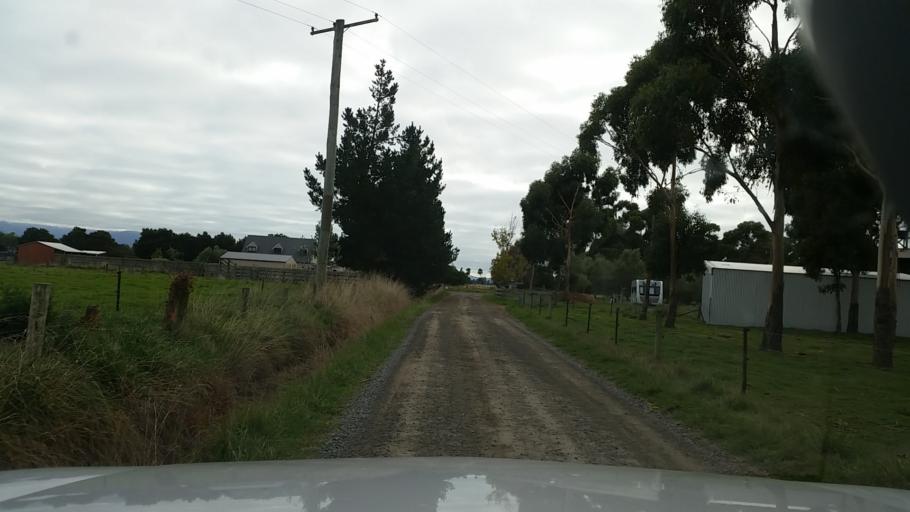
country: NZ
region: Marlborough
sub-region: Marlborough District
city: Blenheim
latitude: -41.5205
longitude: 174.0393
